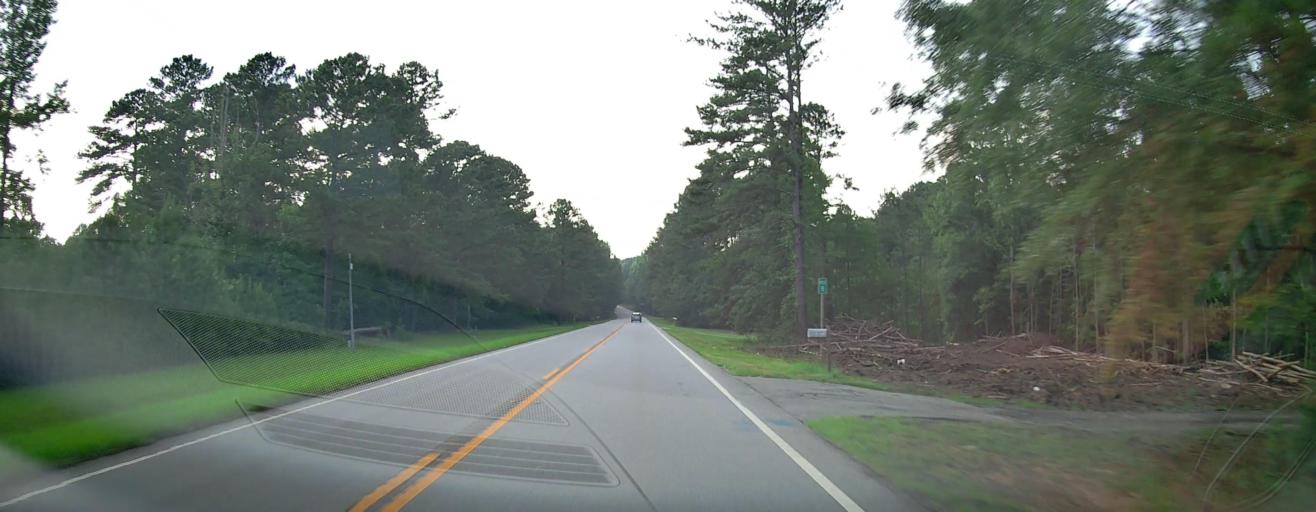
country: US
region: Georgia
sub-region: Monroe County
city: Forsyth
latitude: 33.0607
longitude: -83.7703
